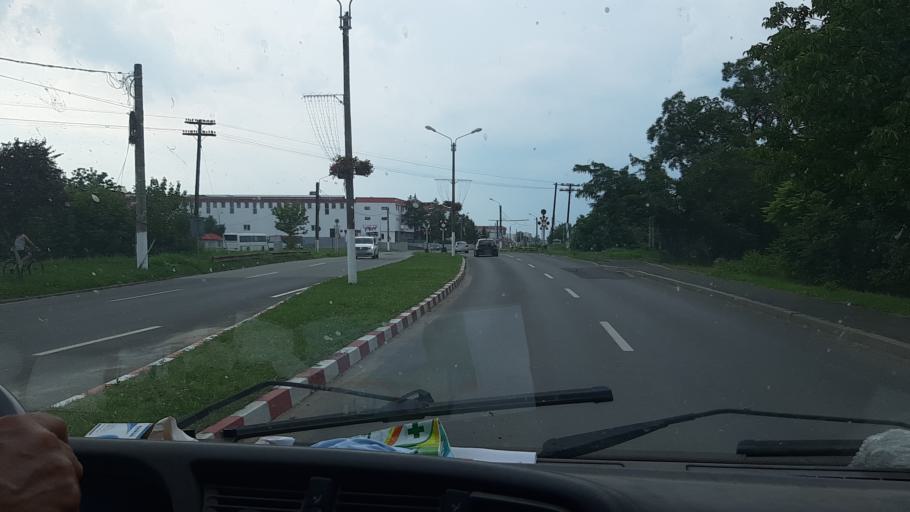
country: RO
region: Timis
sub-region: Municipiul Lugoj
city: Lugoj
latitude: 45.7007
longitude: 21.8942
